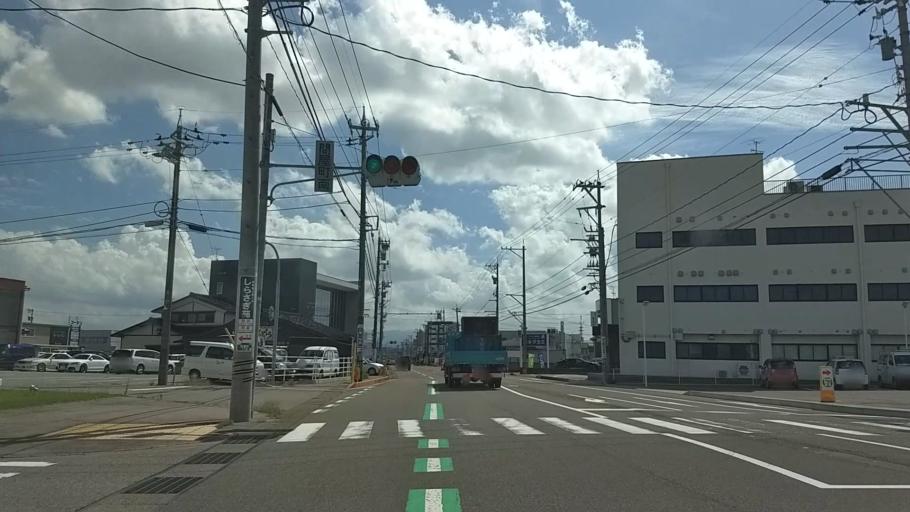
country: JP
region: Ishikawa
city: Kanazawa-shi
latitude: 36.6049
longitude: 136.6353
